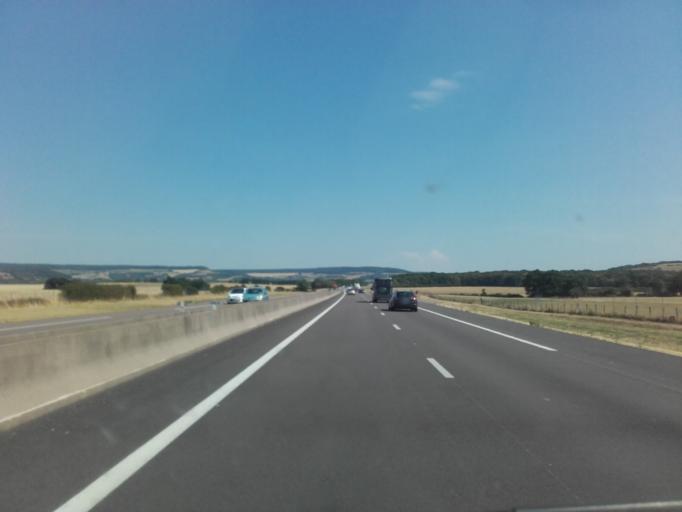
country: FR
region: Bourgogne
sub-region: Departement de la Cote-d'Or
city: Vitteaux
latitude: 47.3562
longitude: 4.4351
